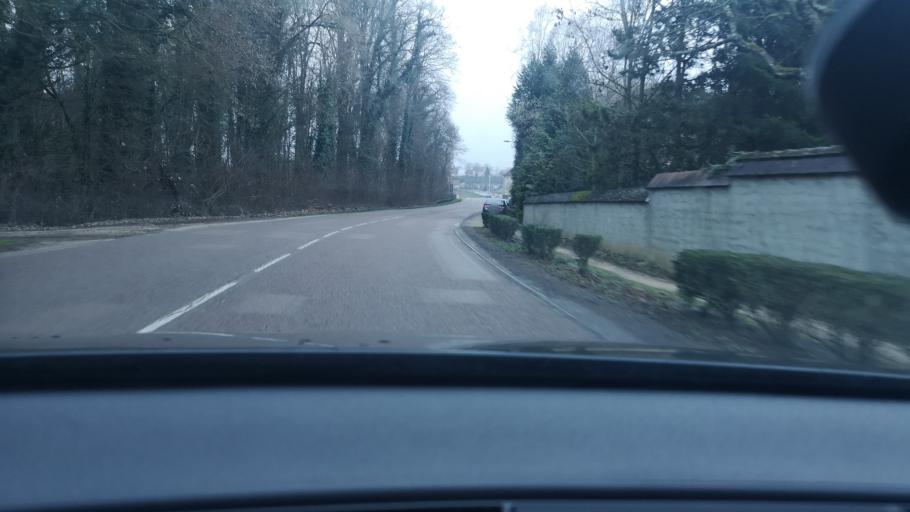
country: FR
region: Bourgogne
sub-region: Departement de la Cote-d'Or
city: Fenay
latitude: 47.2269
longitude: 5.0639
